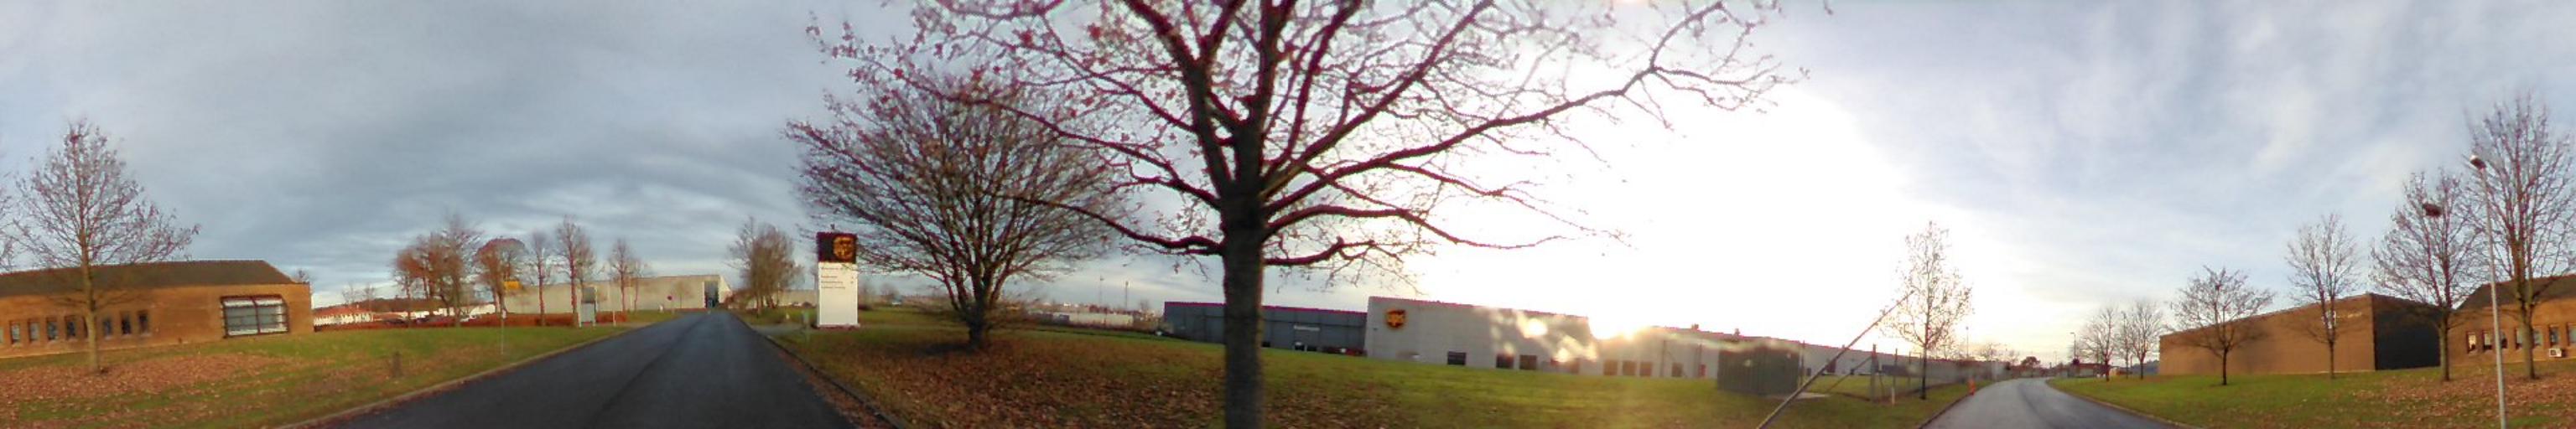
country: DK
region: South Denmark
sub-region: Vejle Kommune
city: Vejle
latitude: 55.6765
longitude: 9.5852
